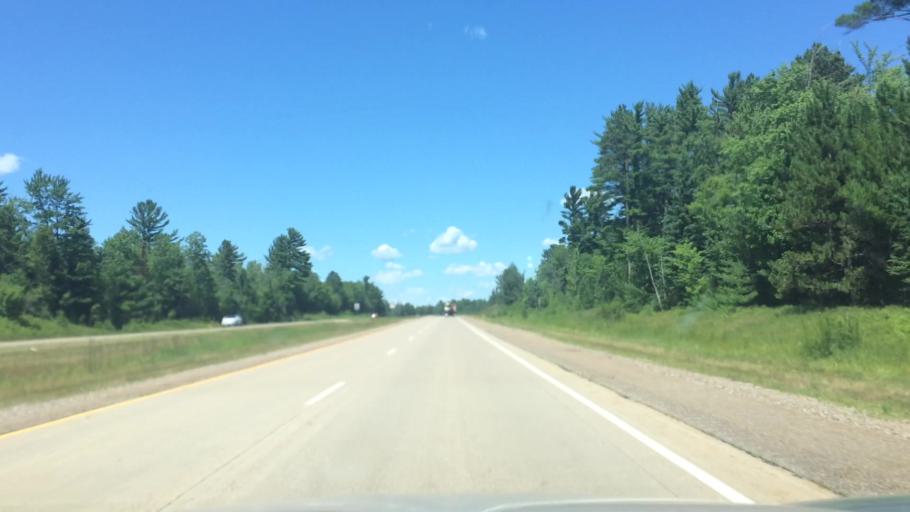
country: US
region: Wisconsin
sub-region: Lincoln County
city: Tomahawk
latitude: 45.4388
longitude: -89.6821
